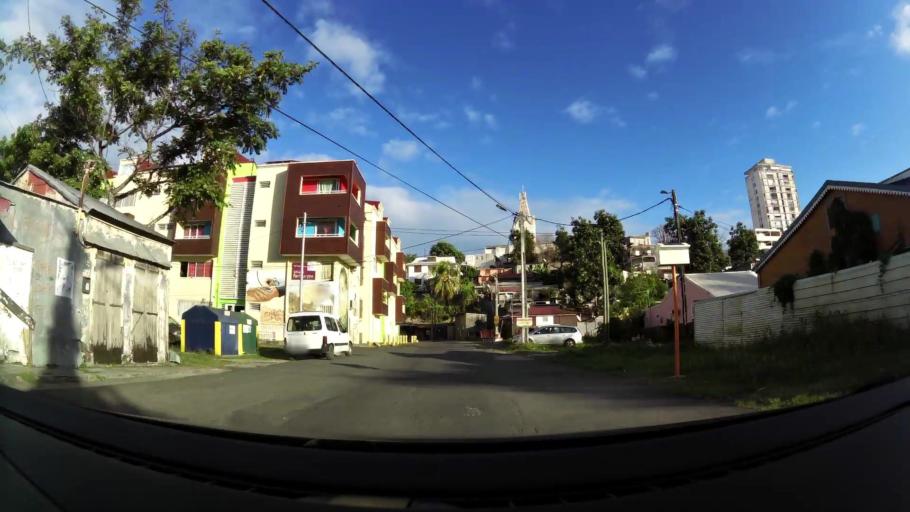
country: GP
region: Guadeloupe
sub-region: Guadeloupe
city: Pointe-a-Pitre
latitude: 16.2340
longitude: -61.5318
